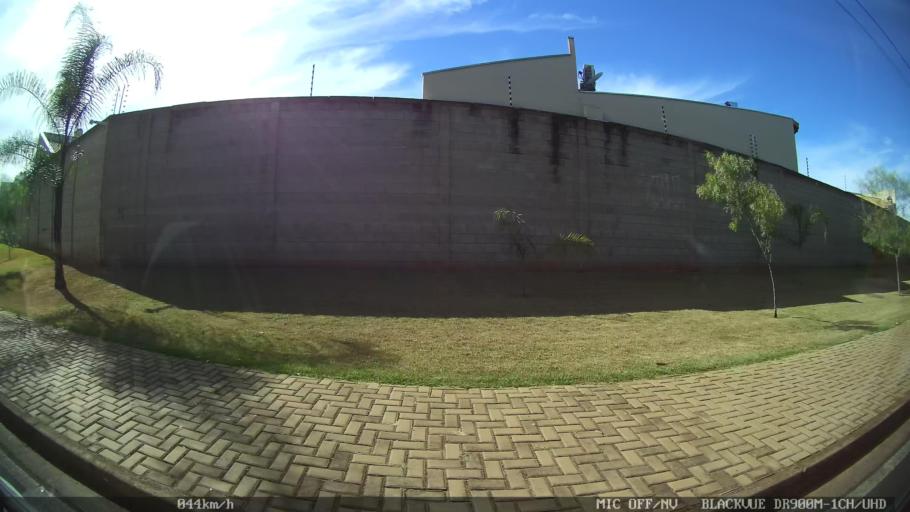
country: BR
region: Sao Paulo
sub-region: Catanduva
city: Catanduva
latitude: -21.1231
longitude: -48.9599
